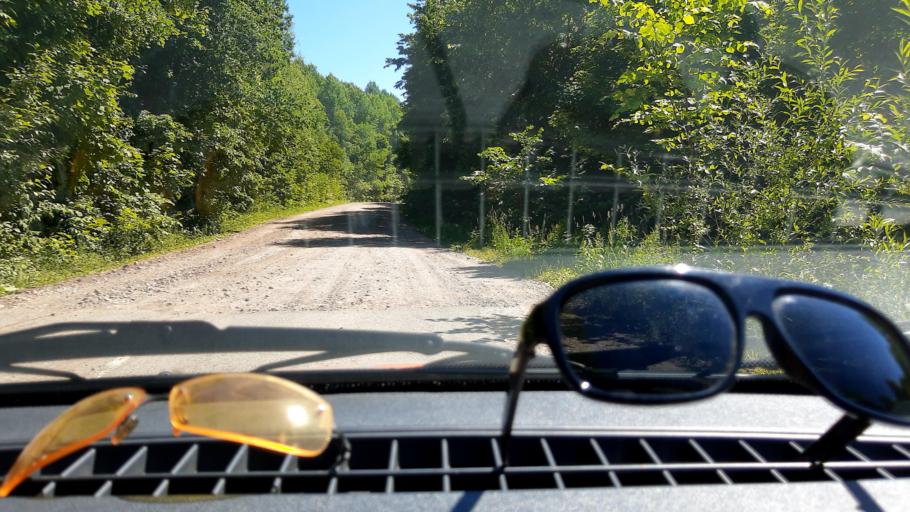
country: RU
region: Bashkortostan
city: Ulu-Telyak
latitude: 54.8068
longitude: 57.0363
